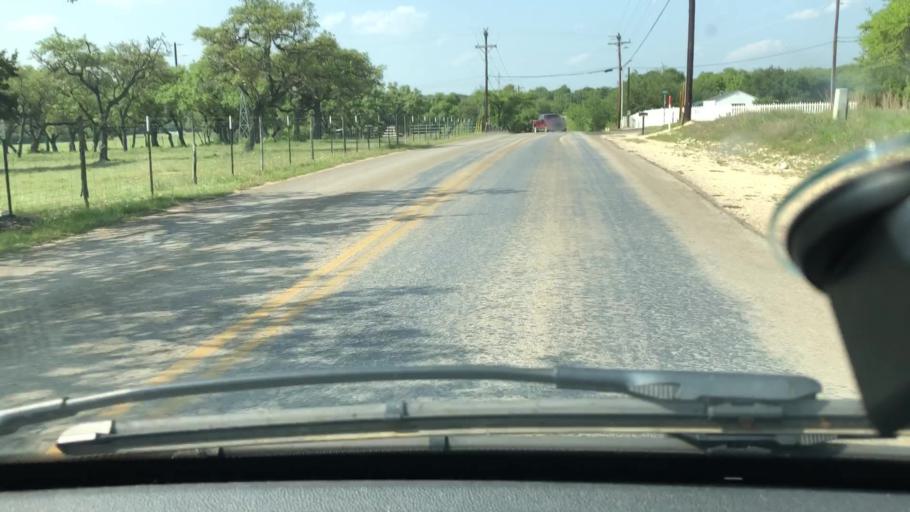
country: US
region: Texas
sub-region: Comal County
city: Bulverde
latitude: 29.7716
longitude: -98.4587
